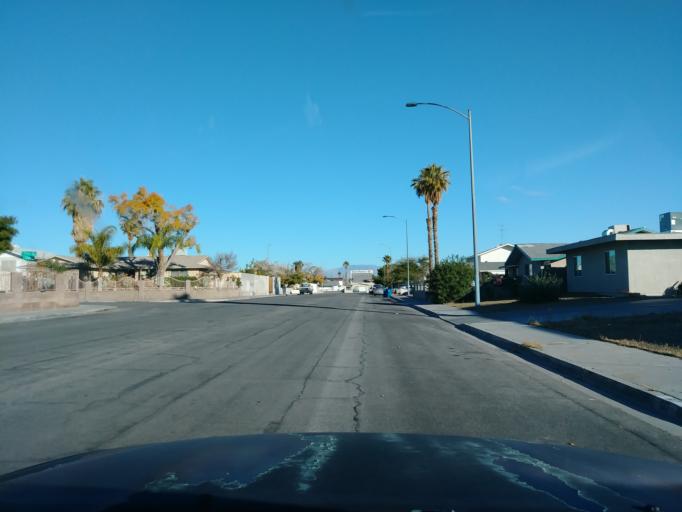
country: US
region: Nevada
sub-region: Clark County
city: Spring Valley
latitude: 36.1647
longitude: -115.2468
